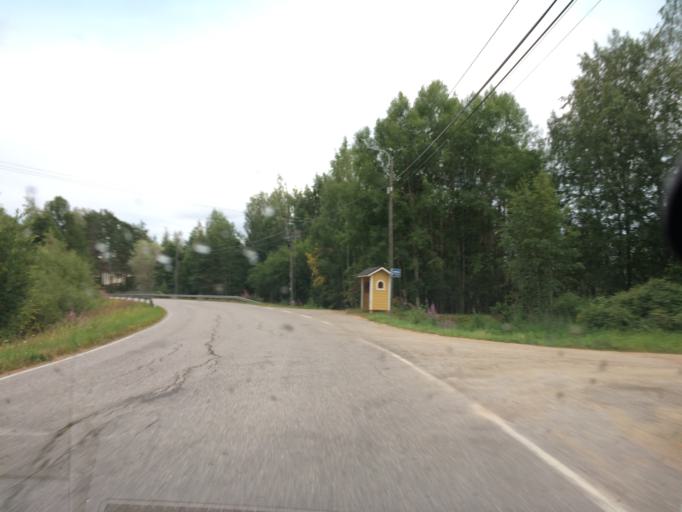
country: FI
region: Haeme
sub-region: Haemeenlinna
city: Tuulos
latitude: 61.1759
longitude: 24.7603
